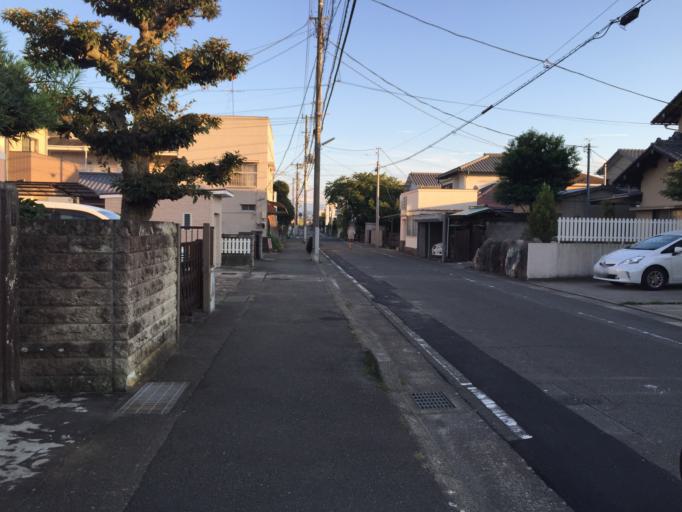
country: JP
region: Shizuoka
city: Numazu
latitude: 35.0926
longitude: 138.8638
